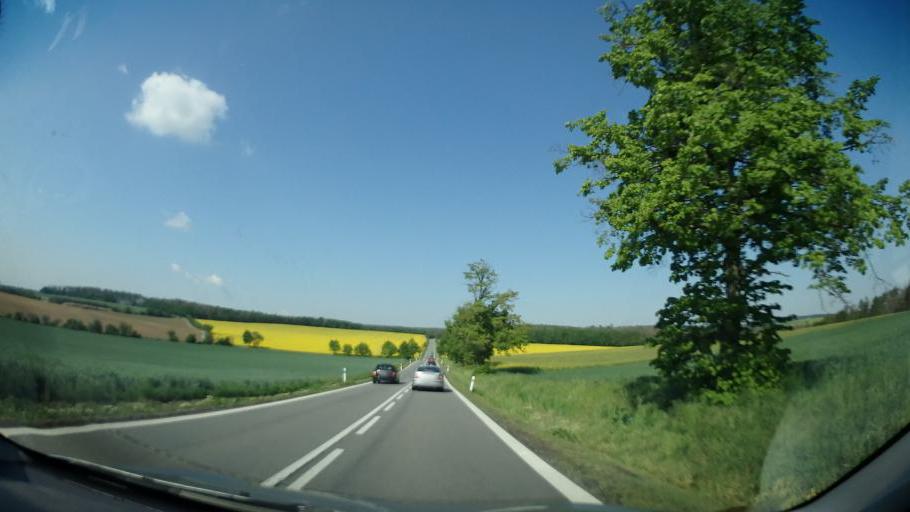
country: CZ
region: South Moravian
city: Zbysov
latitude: 49.1786
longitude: 16.3177
